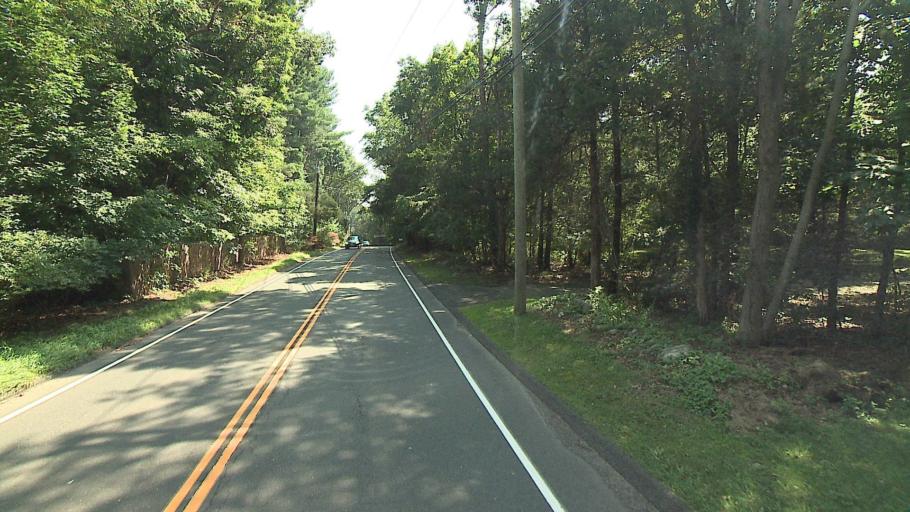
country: US
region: Connecticut
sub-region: Fairfield County
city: Westport
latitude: 41.1806
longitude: -73.3660
